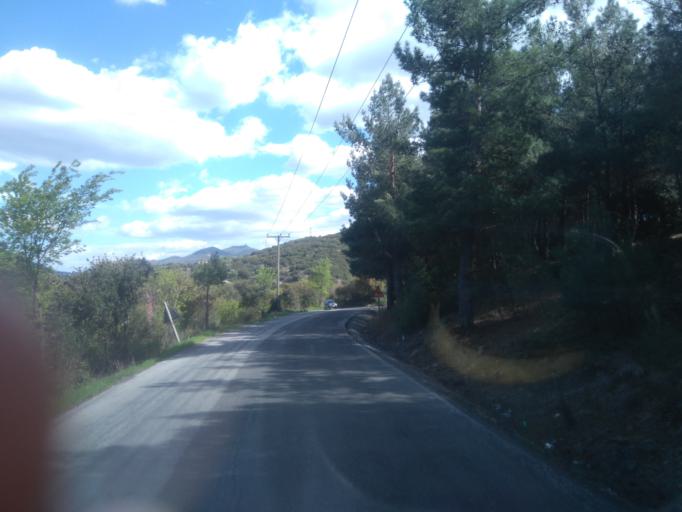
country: GR
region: Central Macedonia
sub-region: Nomos Thessalonikis
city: Asvestochori
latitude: 40.6398
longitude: 23.0129
